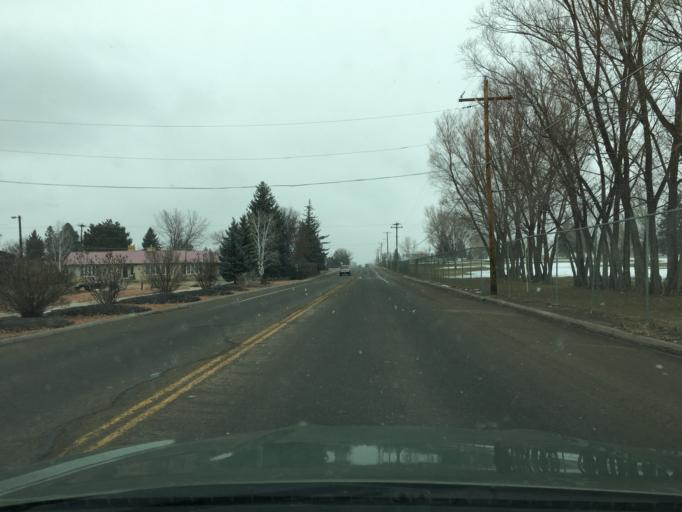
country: US
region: Colorado
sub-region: Montrose County
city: Montrose
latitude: 38.4755
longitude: -107.8566
